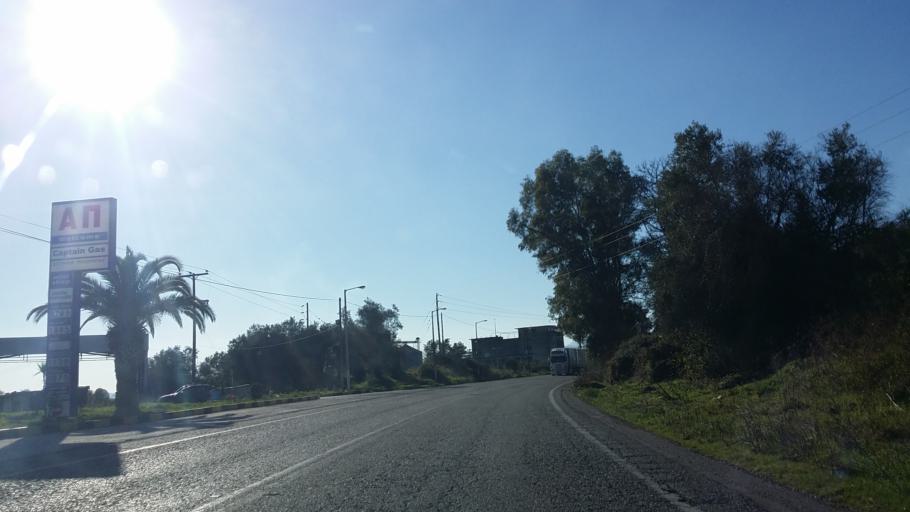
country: GR
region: West Greece
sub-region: Nomos Aitolias kai Akarnanias
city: Neapolis
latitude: 38.6709
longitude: 21.3468
